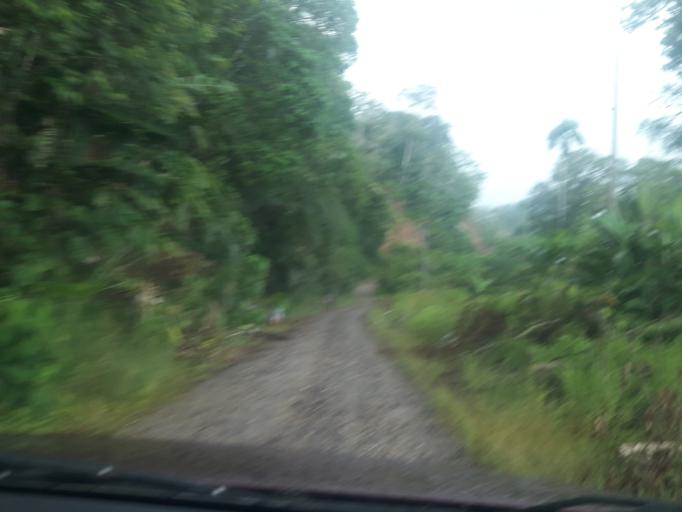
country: EC
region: Napo
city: Tena
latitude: -1.0886
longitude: -77.7067
